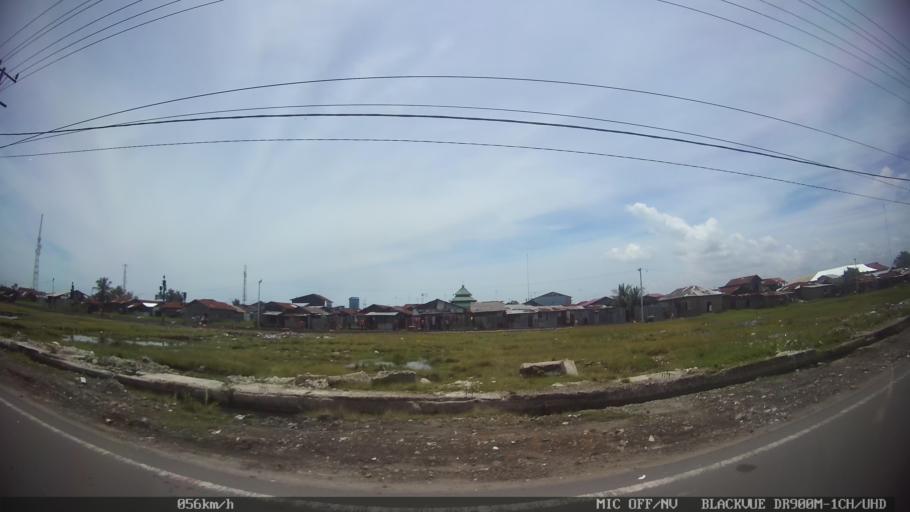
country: ID
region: North Sumatra
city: Belawan
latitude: 3.7774
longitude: 98.6813
